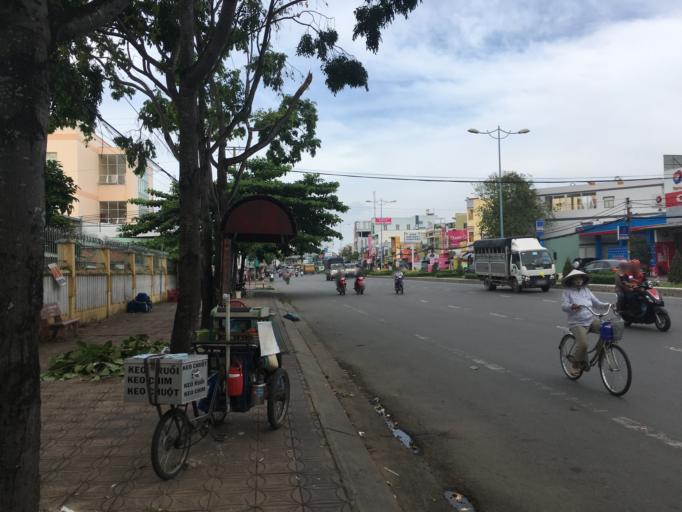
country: VN
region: Can Tho
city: Can Tho
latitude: 10.0308
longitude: 105.7728
